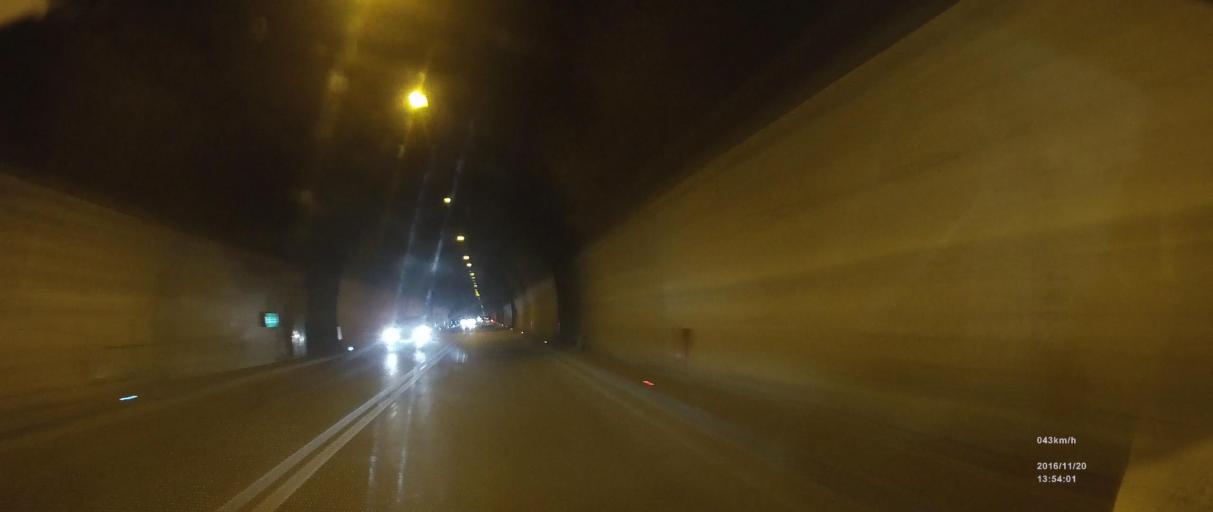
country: HR
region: Splitsko-Dalmatinska
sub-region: Grad Split
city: Split
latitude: 43.5113
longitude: 16.4271
